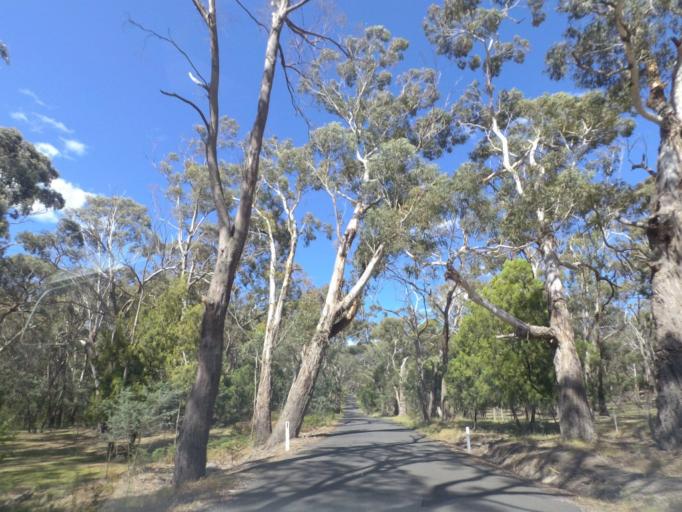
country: AU
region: Victoria
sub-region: Hume
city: Sunbury
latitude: -37.4204
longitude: 144.6254
